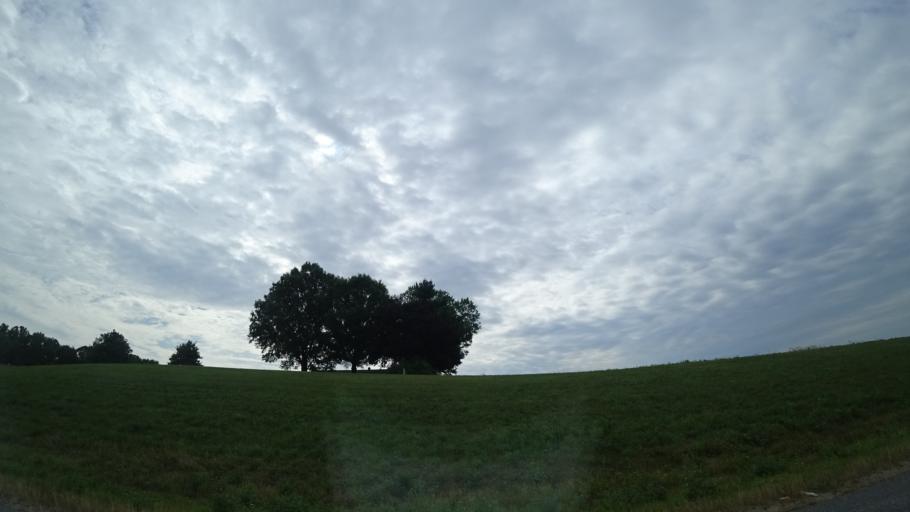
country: US
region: Virginia
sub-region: Spotsylvania County
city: Spotsylvania
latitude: 38.1852
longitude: -77.6206
